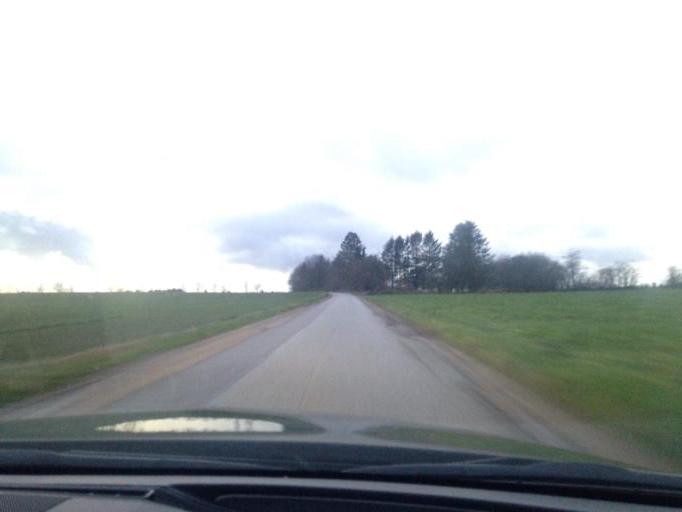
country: DK
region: South Denmark
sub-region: Kolding Kommune
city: Kolding
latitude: 55.5670
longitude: 9.4589
